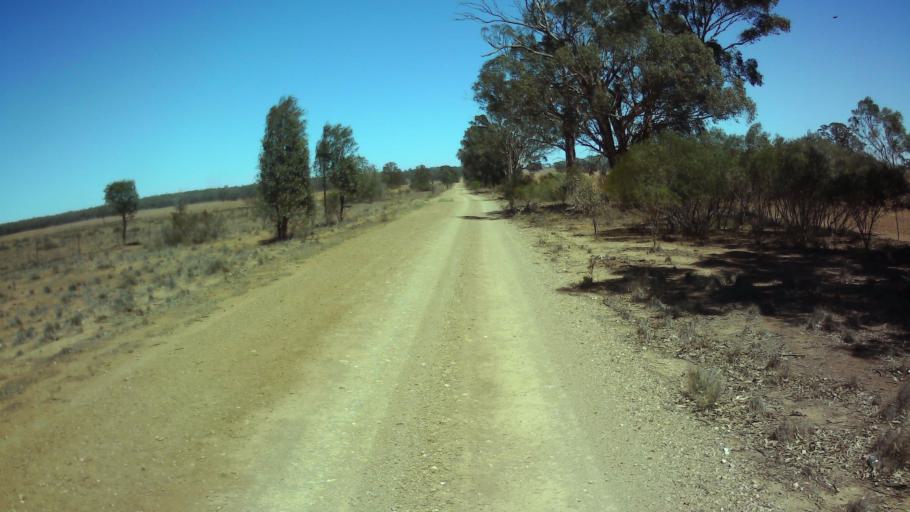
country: AU
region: New South Wales
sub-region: Forbes
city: Forbes
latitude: -33.6996
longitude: 147.8652
